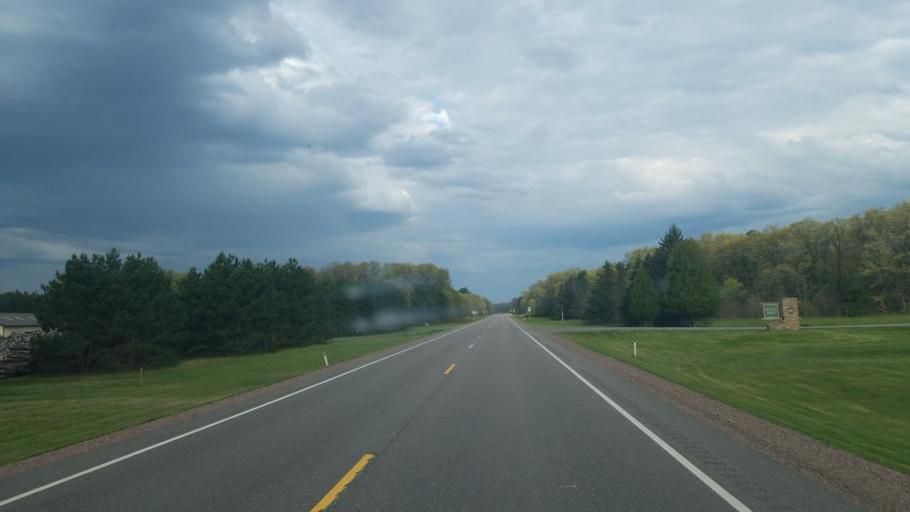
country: US
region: Wisconsin
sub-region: Wood County
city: Nekoosa
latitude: 44.3787
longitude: -90.1249
